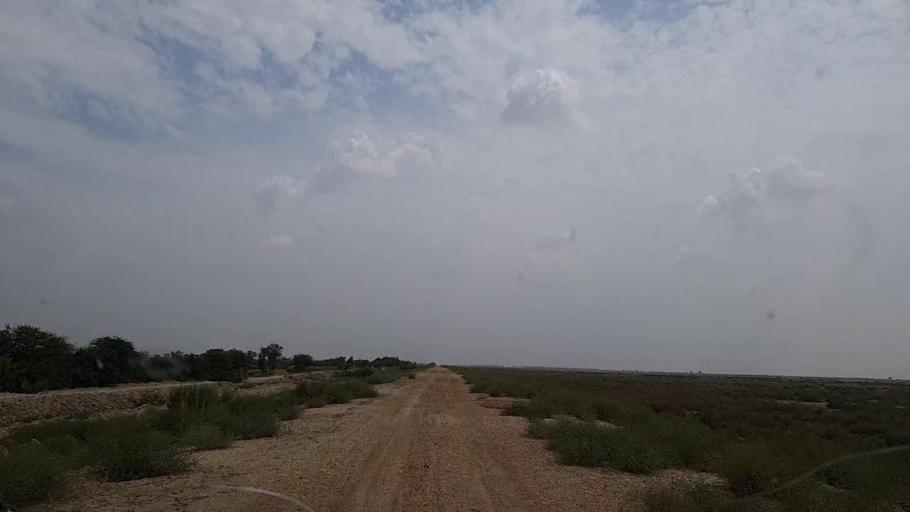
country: PK
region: Sindh
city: Johi
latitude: 26.7950
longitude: 67.6015
